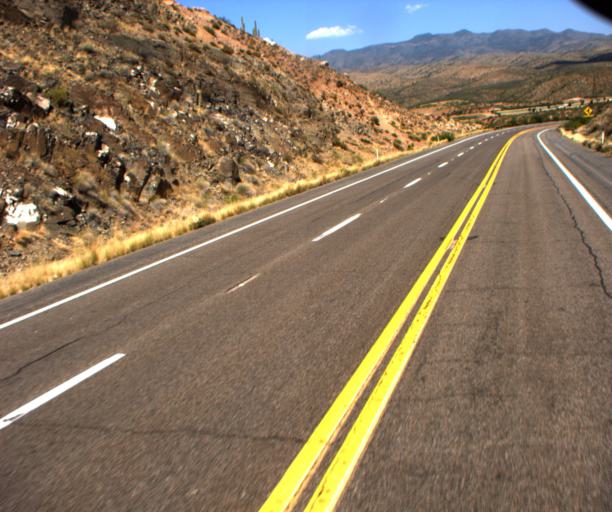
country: US
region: Arizona
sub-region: Gila County
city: Claypool
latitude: 33.5207
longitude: -110.8764
